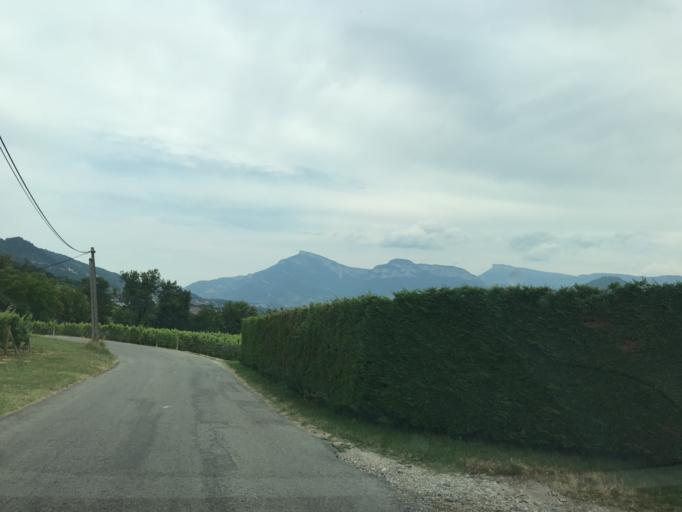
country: FR
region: Rhone-Alpes
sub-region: Departement de la Savoie
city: Saint-Baldoph
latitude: 45.5029
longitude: 5.9581
